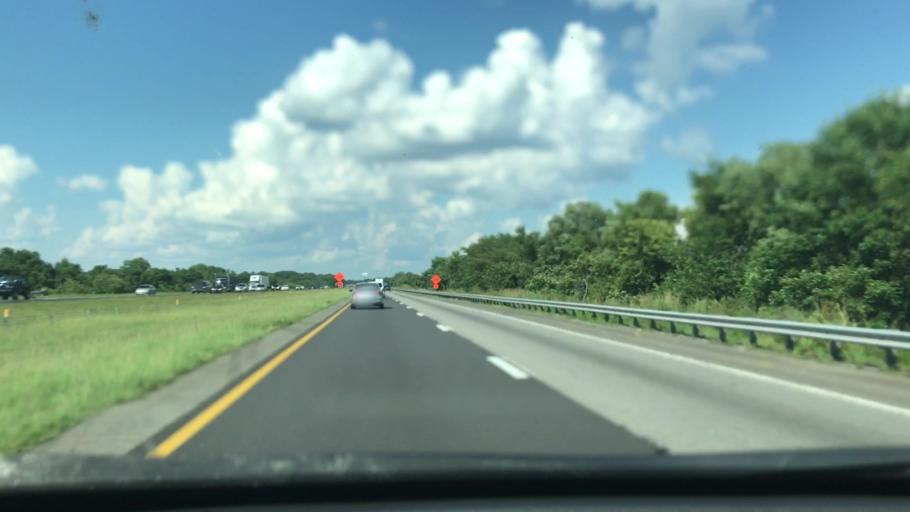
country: US
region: South Carolina
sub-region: Orangeburg County
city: Holly Hill
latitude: 33.5106
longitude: -80.4454
